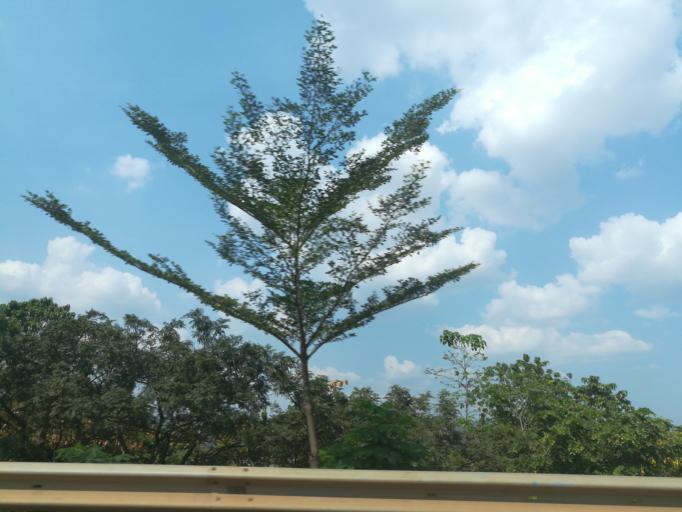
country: NG
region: Abuja Federal Capital Territory
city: Abuja
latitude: 9.0793
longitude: 7.4273
